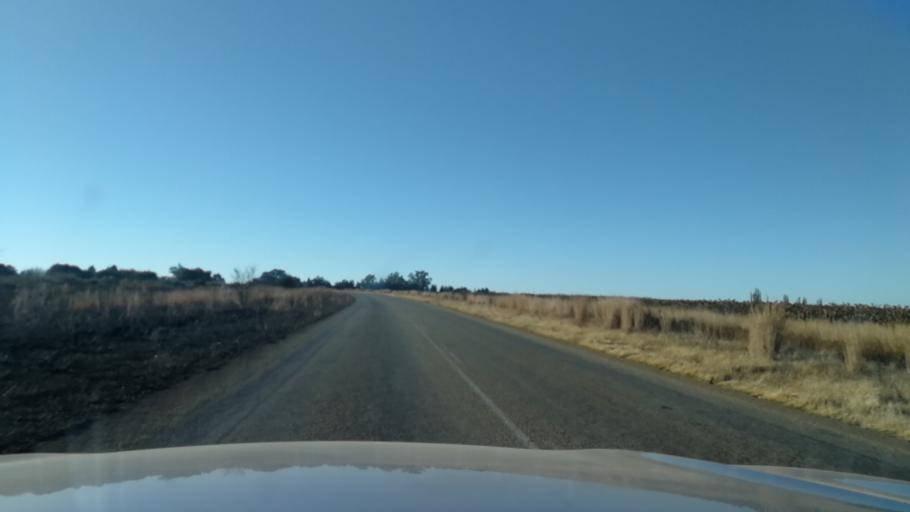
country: ZA
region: North-West
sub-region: Bojanala Platinum District Municipality
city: Rustenburg
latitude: -25.9494
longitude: 27.1778
